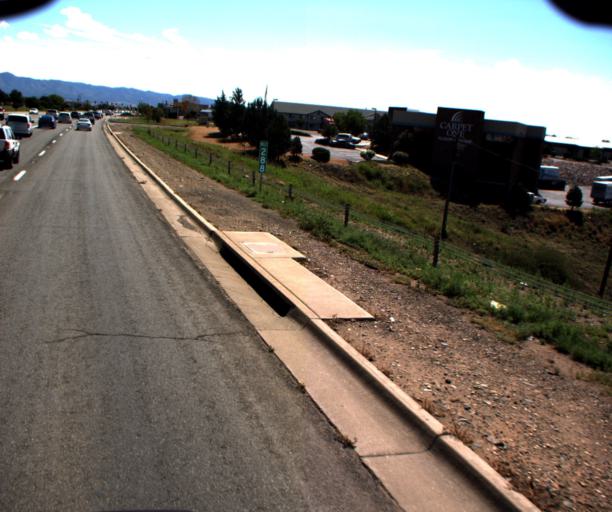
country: US
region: Arizona
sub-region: Yavapai County
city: Prescott Valley
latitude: 34.5852
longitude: -112.3310
